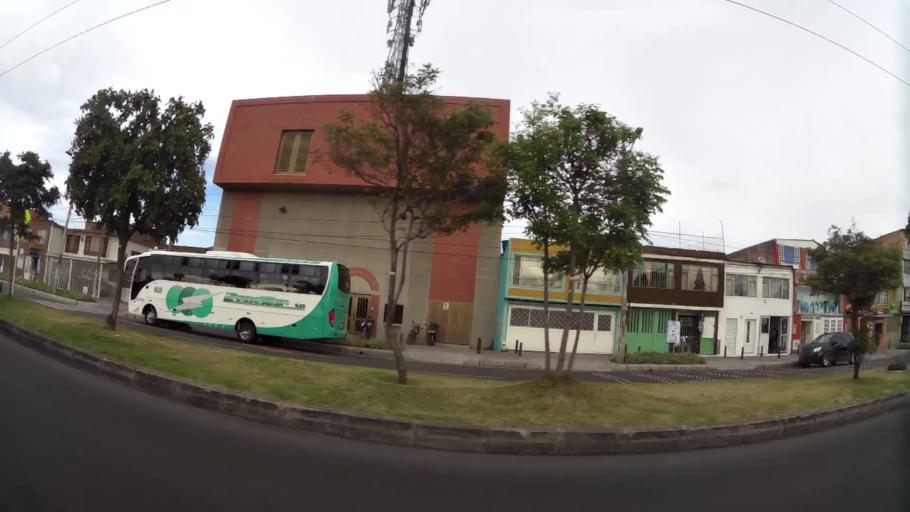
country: CO
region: Cundinamarca
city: Soacha
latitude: 4.6177
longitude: -74.1562
